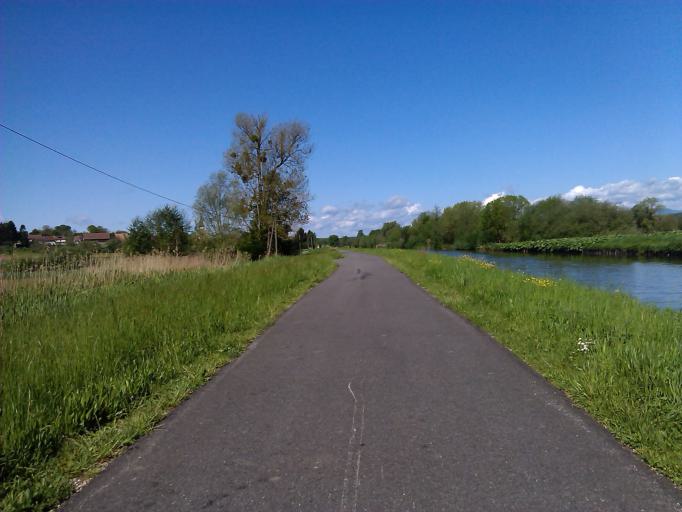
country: FR
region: Alsace
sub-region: Departement du Haut-Rhin
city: Aspach
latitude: 47.6657
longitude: 7.1922
